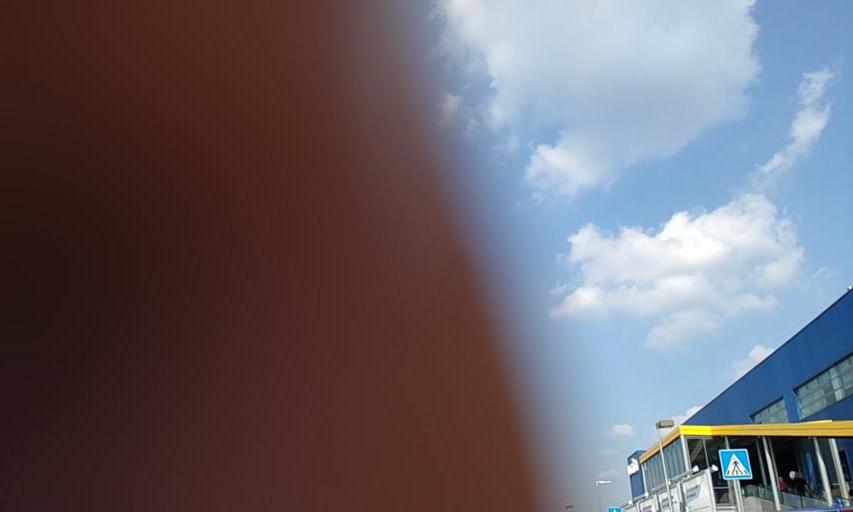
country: IT
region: Piedmont
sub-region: Provincia di Torino
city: Collegno
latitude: 45.0984
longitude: 7.5805
